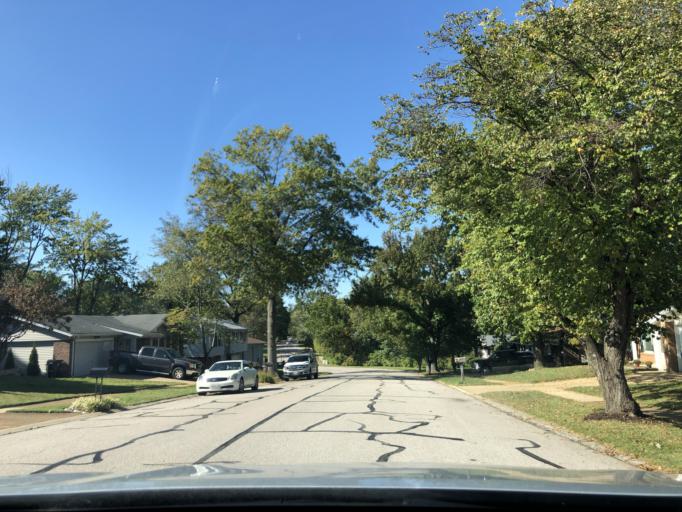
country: US
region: Missouri
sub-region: Saint Louis County
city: Concord
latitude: 38.4969
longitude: -90.3669
